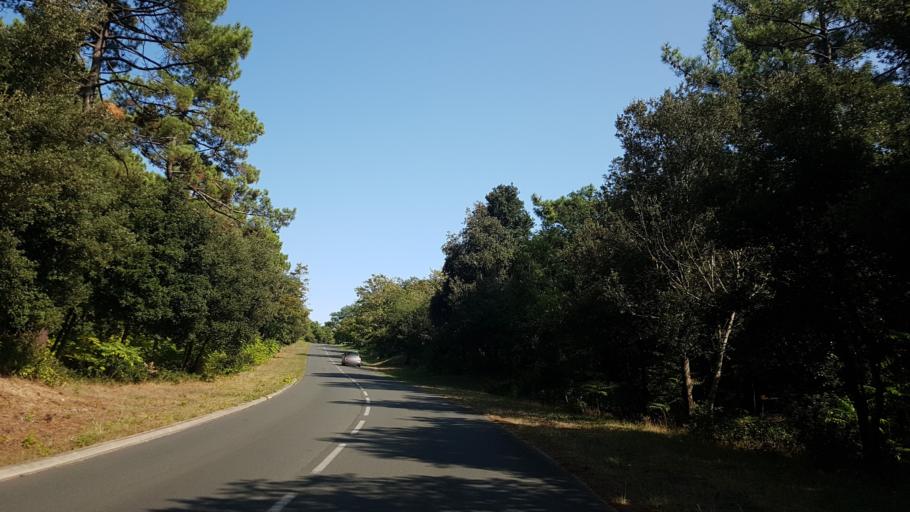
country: FR
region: Poitou-Charentes
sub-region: Departement de la Charente-Maritime
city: Les Mathes
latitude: 45.6980
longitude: -1.2184
